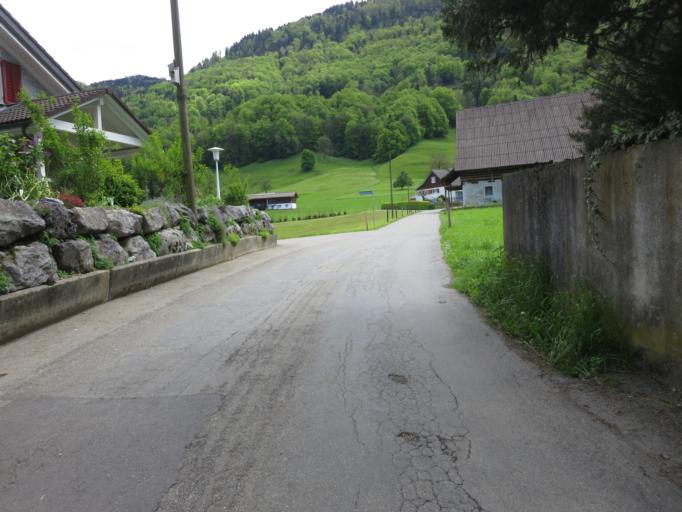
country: CH
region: Schwyz
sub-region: Bezirk March
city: Schubelbach
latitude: 47.1716
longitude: 8.9262
